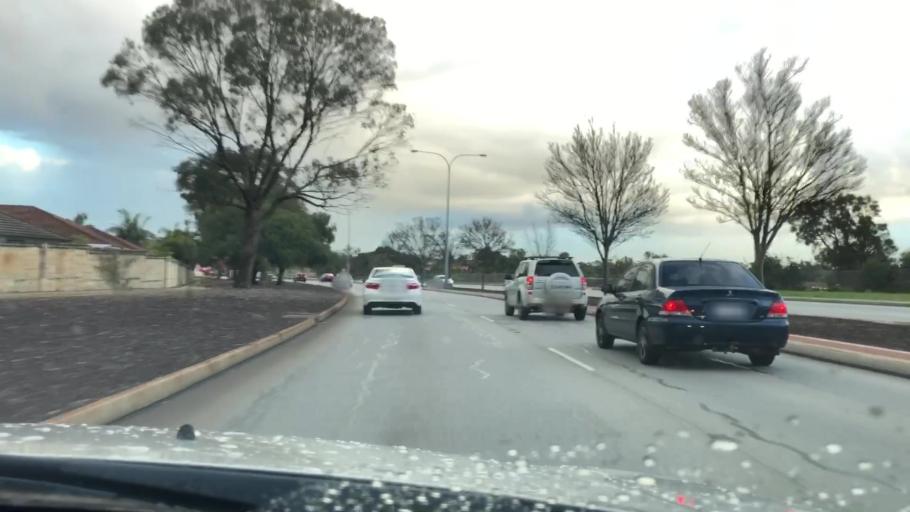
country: AU
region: Western Australia
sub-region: Armadale
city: Harrisdale
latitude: -32.0948
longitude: 115.9290
